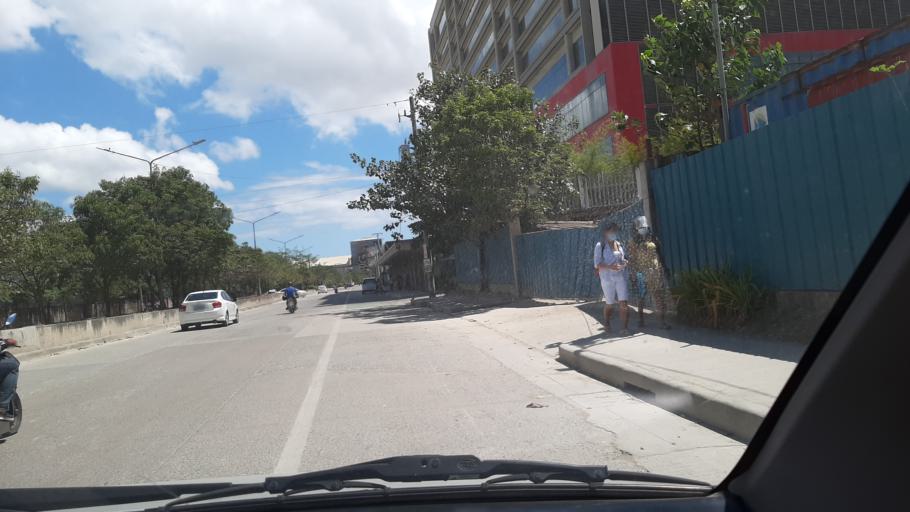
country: PH
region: Central Visayas
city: Mandaue City
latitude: 10.3224
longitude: 123.9306
